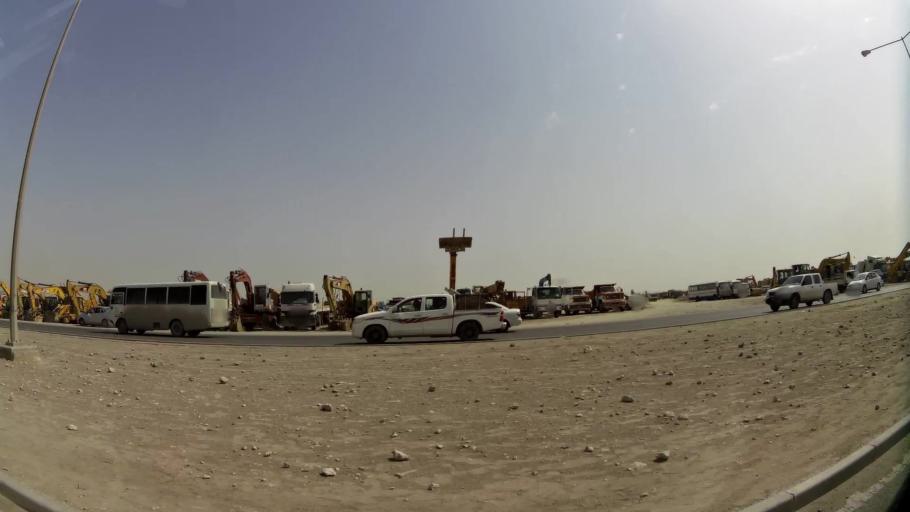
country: QA
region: Al Wakrah
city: Al Wukayr
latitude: 25.1789
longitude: 51.4648
